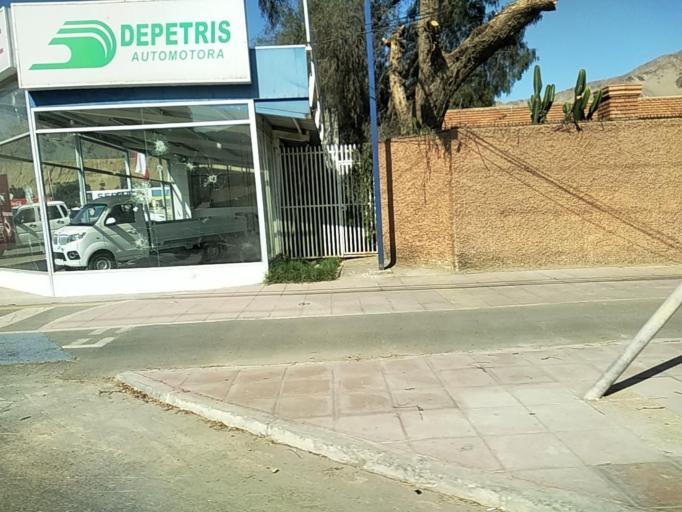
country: CL
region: Atacama
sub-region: Provincia de Copiapo
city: Copiapo
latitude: -27.3635
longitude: -70.3450
